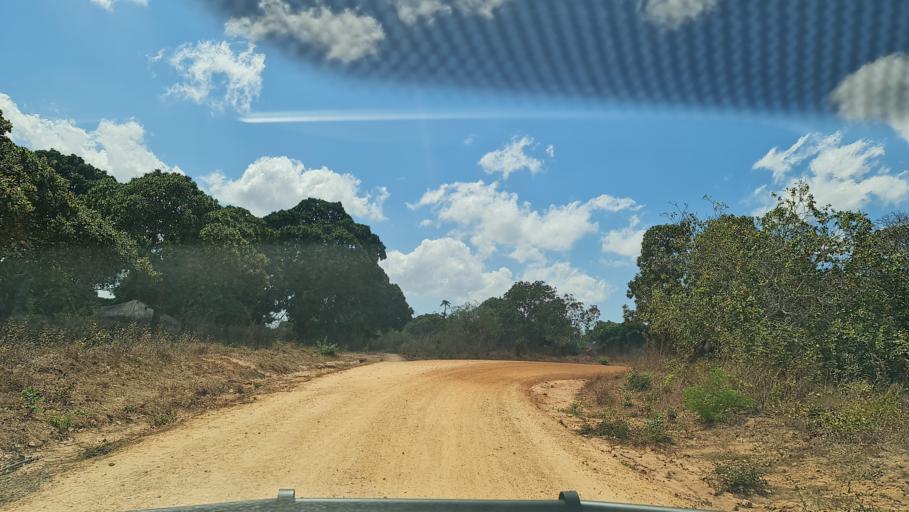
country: MZ
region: Nampula
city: Nacala
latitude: -14.1694
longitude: 40.2568
